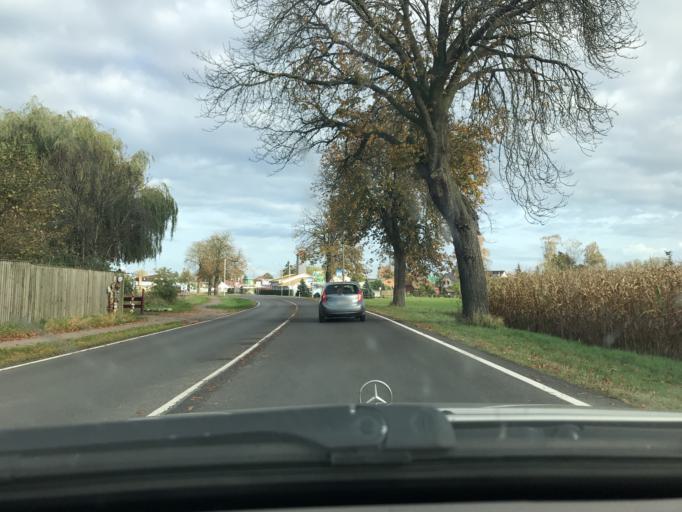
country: DE
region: Mecklenburg-Vorpommern
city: Karlshagen
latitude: 54.0650
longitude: 13.8489
